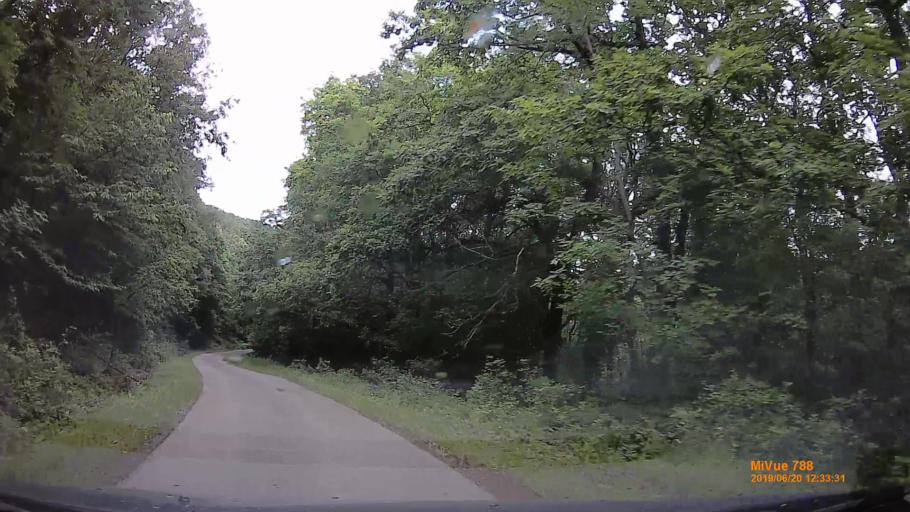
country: HU
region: Baranya
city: Hosszuheteny
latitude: 46.1932
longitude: 18.3663
